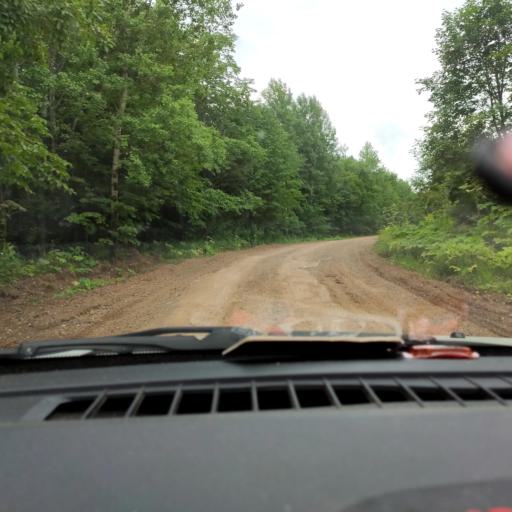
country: RU
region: Perm
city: Kultayevo
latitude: 57.8112
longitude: 56.0043
